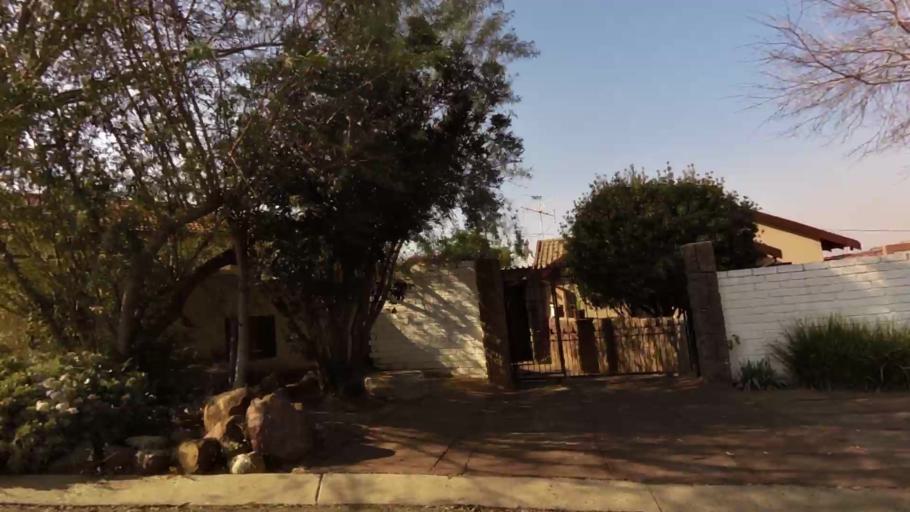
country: ZA
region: Gauteng
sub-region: City of Johannesburg Metropolitan Municipality
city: Soweto
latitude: -26.2892
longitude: 27.9527
